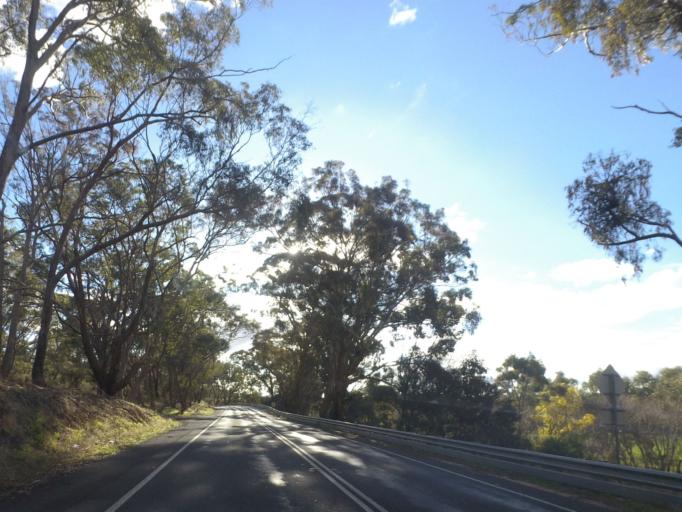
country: AU
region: Victoria
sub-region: Mount Alexander
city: Castlemaine
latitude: -37.1002
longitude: 144.2947
